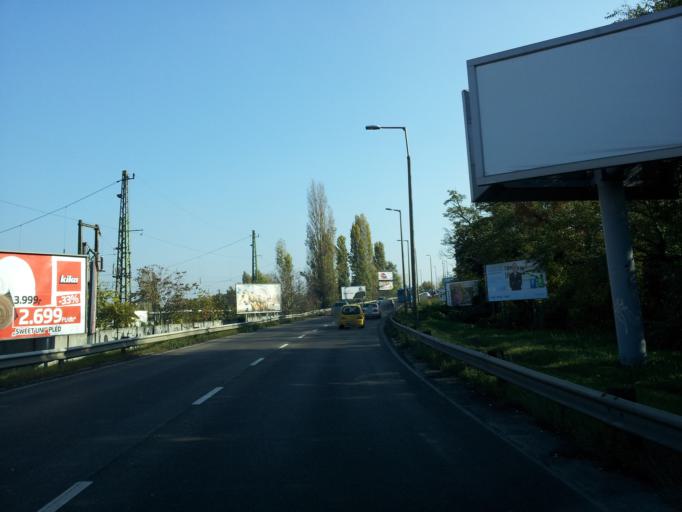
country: HU
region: Budapest
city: Budapest XIX. keruelet
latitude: 47.4621
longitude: 19.1554
